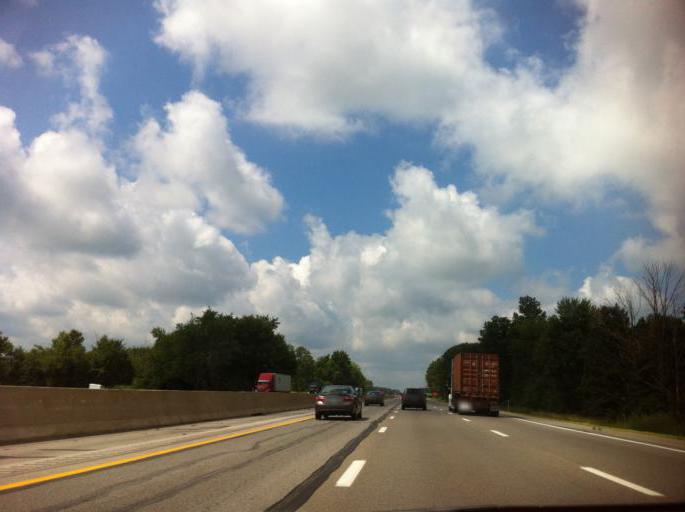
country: US
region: Ohio
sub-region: Huron County
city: Wakeman
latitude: 41.3322
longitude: -82.4358
